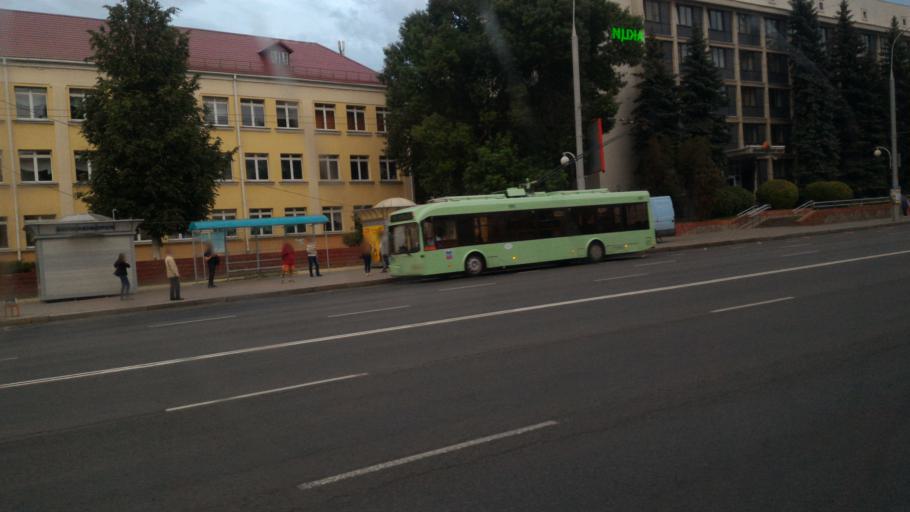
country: BY
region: Minsk
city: Minsk
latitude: 53.8793
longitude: 27.5344
